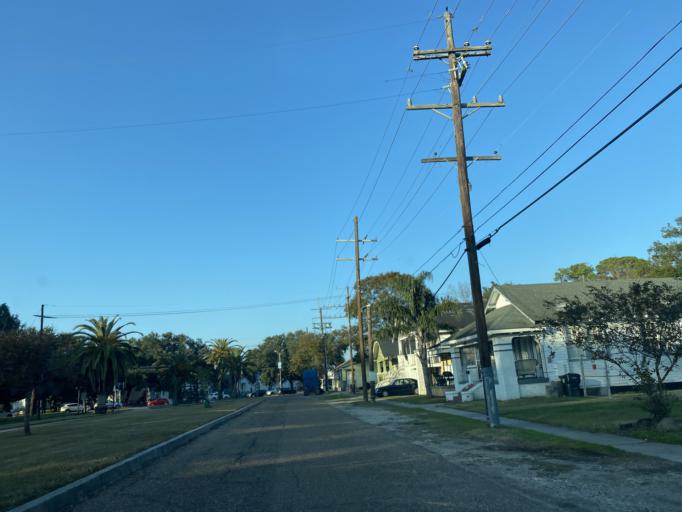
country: US
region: Louisiana
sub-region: Orleans Parish
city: New Orleans
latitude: 29.9940
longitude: -90.0635
